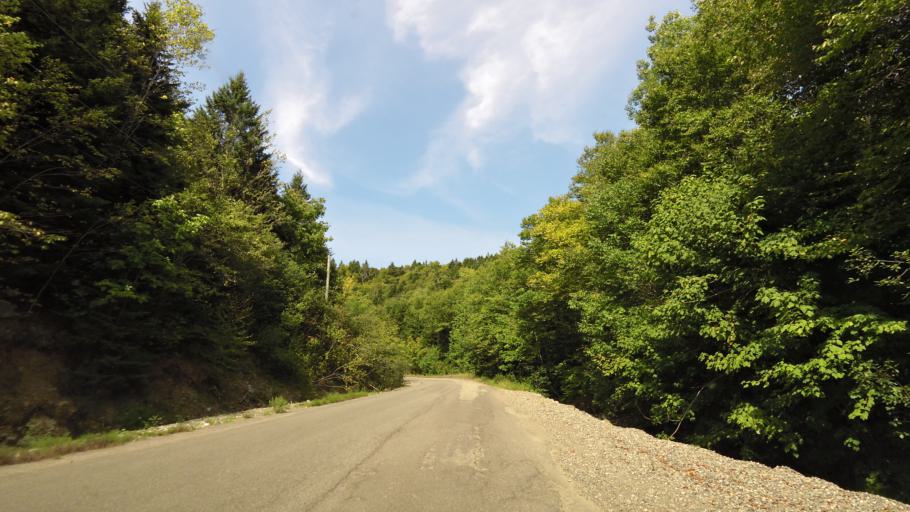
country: CA
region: New Brunswick
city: Hampton
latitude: 45.5506
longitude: -65.8380
